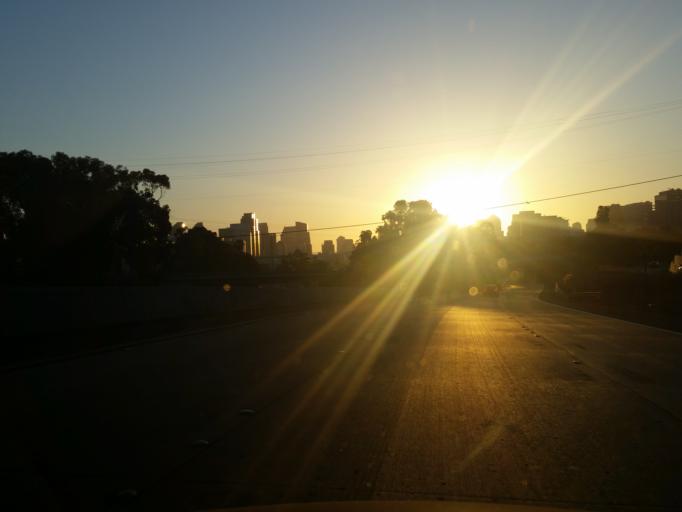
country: US
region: California
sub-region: San Diego County
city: San Diego
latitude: 32.7134
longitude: -117.1440
